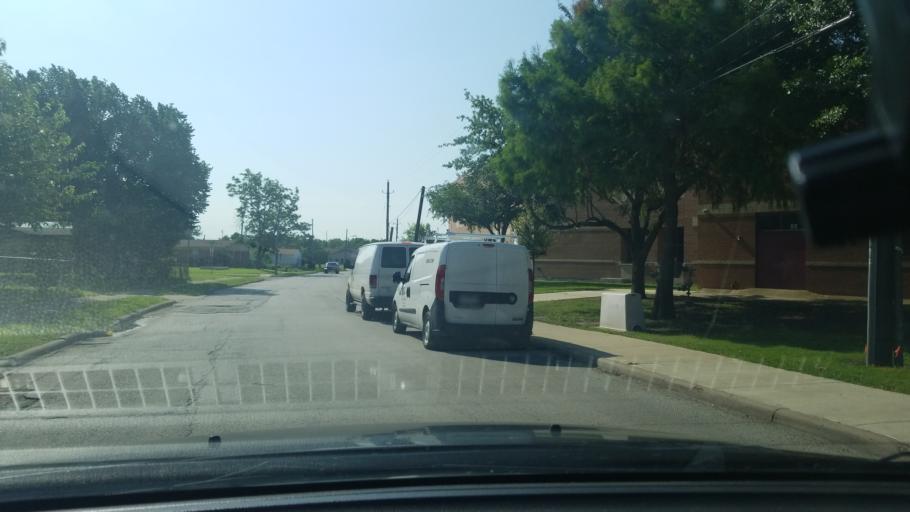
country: US
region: Texas
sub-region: Dallas County
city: Mesquite
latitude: 32.8284
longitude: -96.6451
